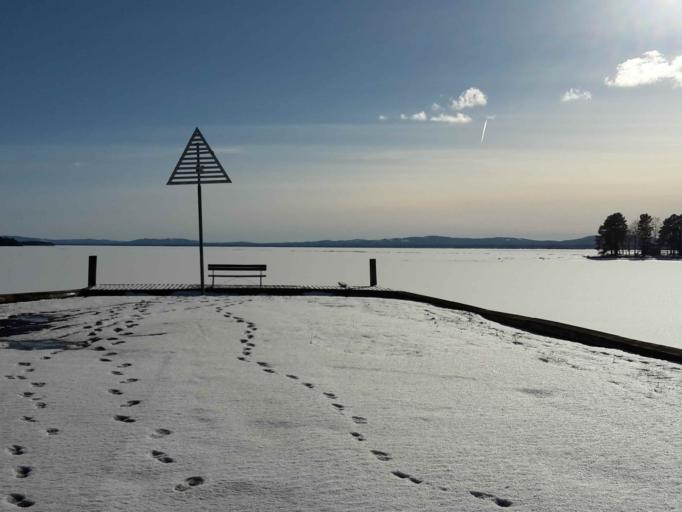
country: SE
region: Dalarna
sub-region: Orsa Kommun
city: Orsa
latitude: 61.1164
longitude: 14.6056
